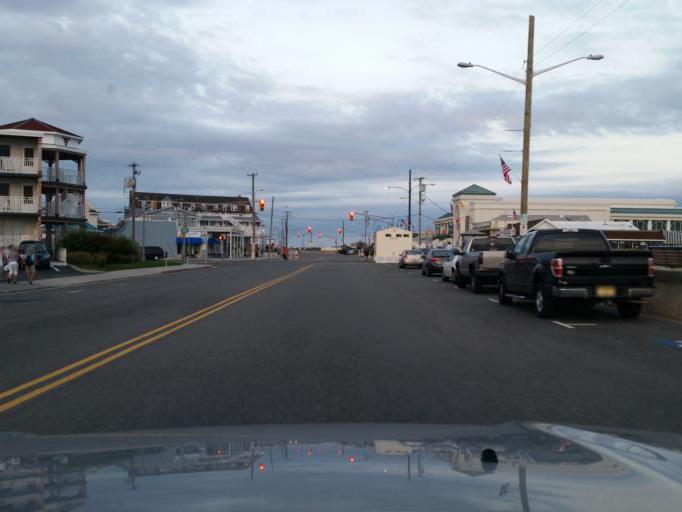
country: US
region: New Jersey
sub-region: Cape May County
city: Cape May
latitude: 38.9305
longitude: -74.9193
